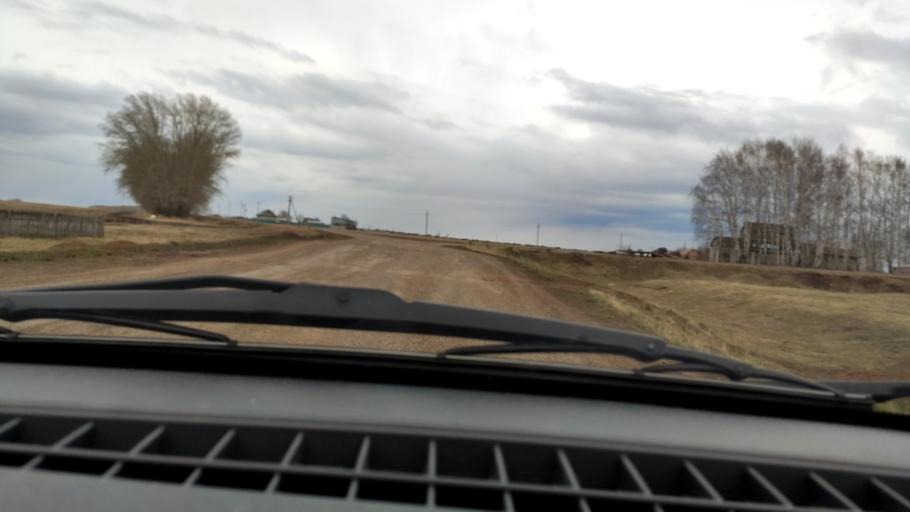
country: RU
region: Bashkortostan
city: Semiletka
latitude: 55.2886
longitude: 54.6669
